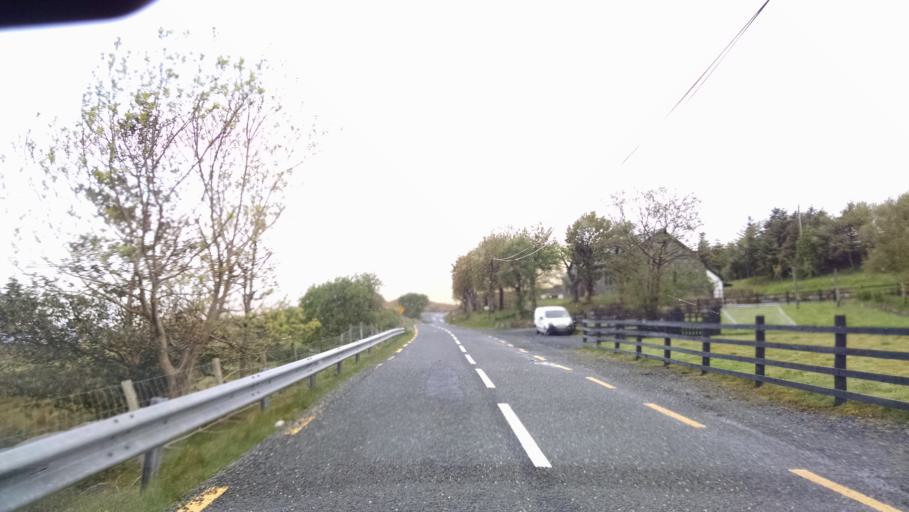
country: IE
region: Connaught
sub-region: Maigh Eo
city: Westport
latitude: 53.6043
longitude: -9.7386
